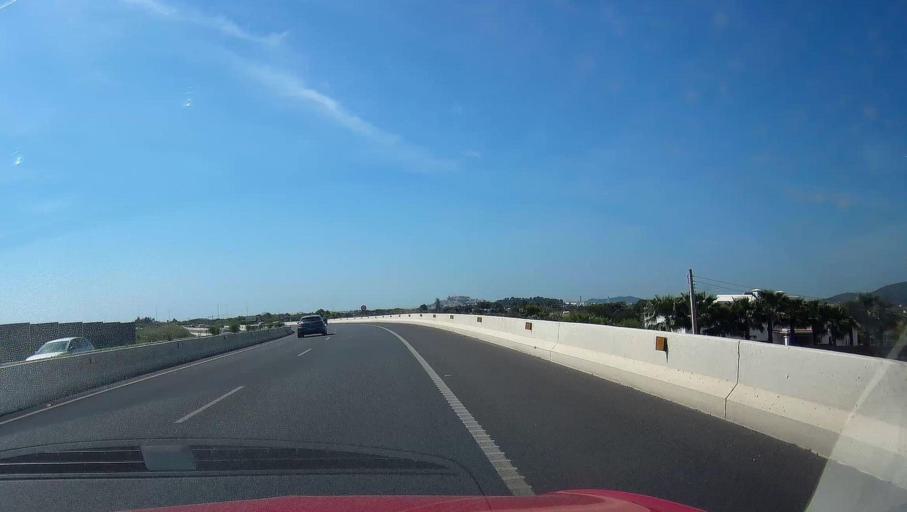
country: ES
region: Balearic Islands
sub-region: Illes Balears
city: Ibiza
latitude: 38.9455
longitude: 1.4432
